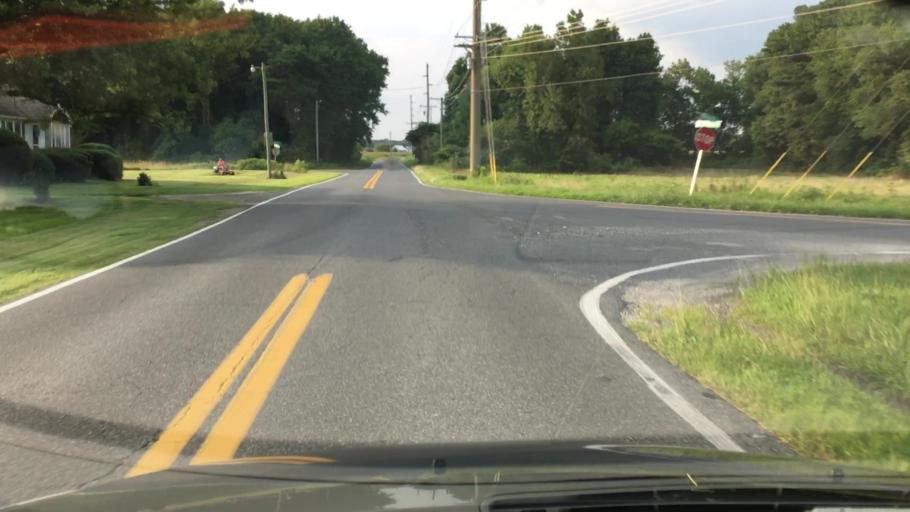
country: US
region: Delaware
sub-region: Sussex County
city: Ocean View
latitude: 38.4939
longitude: -75.1308
